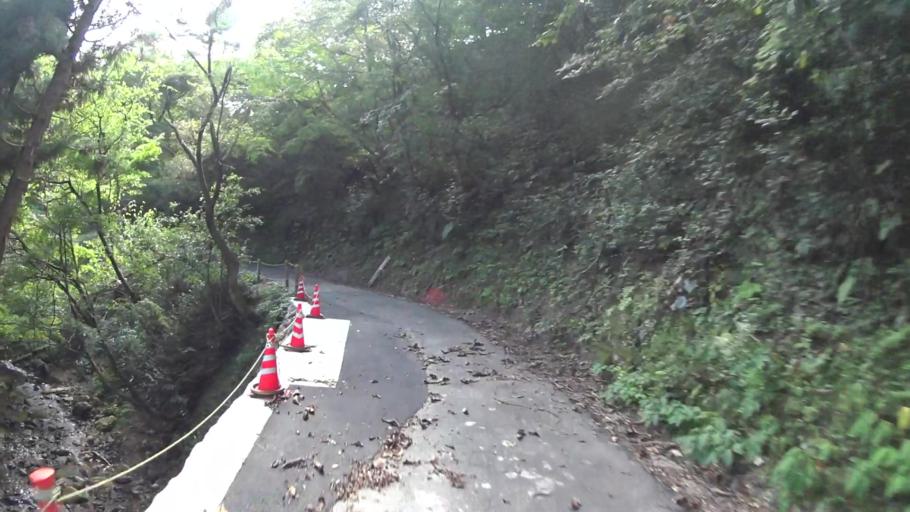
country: JP
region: Kyoto
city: Miyazu
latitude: 35.6722
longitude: 135.1435
